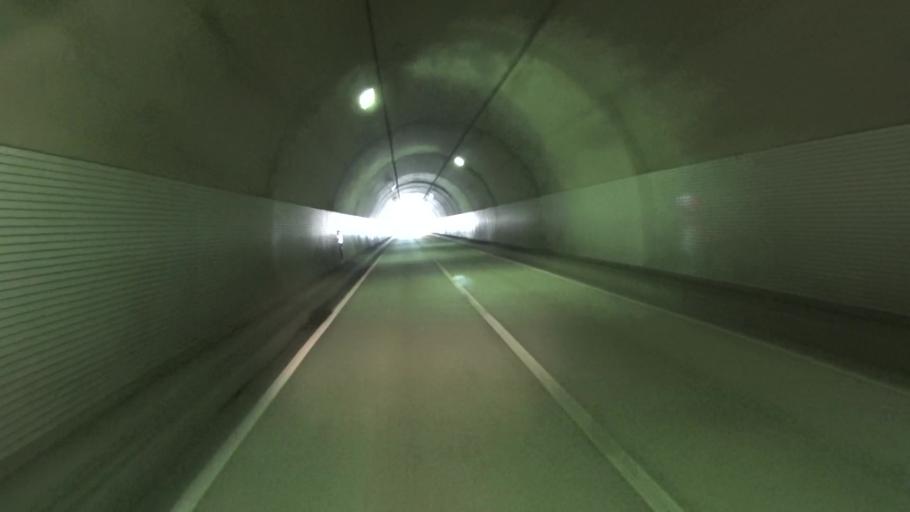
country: JP
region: Kyoto
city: Kameoka
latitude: 35.1089
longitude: 135.5604
